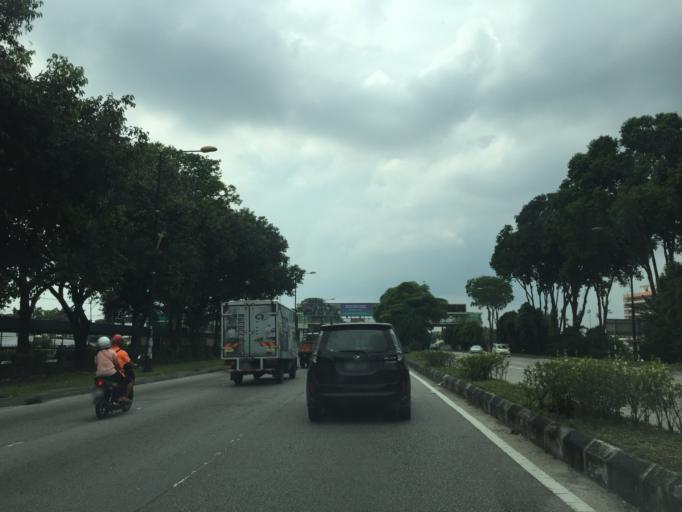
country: MY
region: Selangor
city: Klang
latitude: 3.0224
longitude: 101.4425
